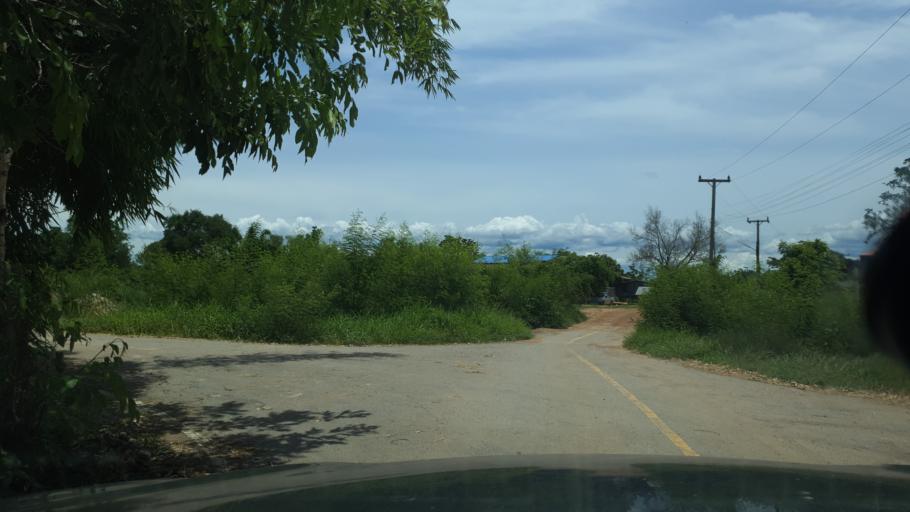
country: TH
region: Sukhothai
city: Ban Na
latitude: 17.1287
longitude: 99.6722
